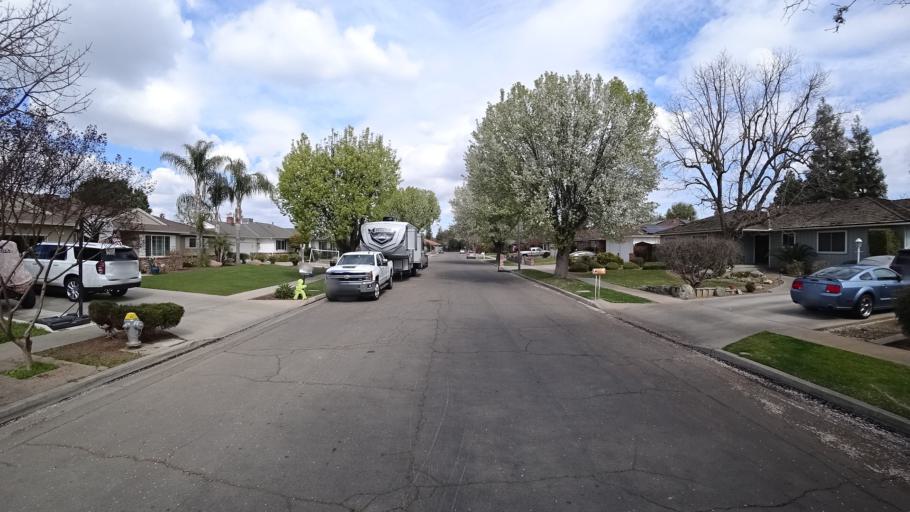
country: US
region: California
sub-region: Fresno County
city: Fresno
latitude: 36.8212
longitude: -119.8506
